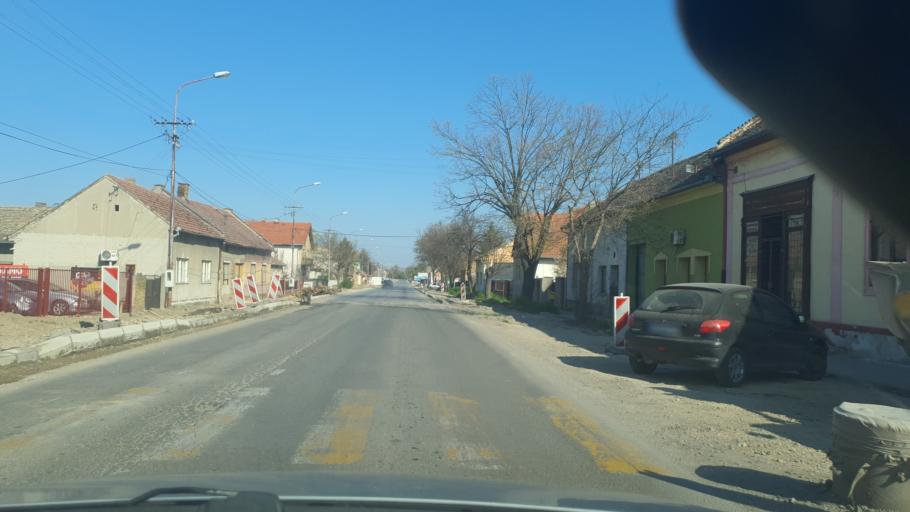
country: RS
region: Autonomna Pokrajina Vojvodina
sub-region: Zapadnobacki Okrug
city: Kula
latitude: 45.6162
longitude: 19.5235
